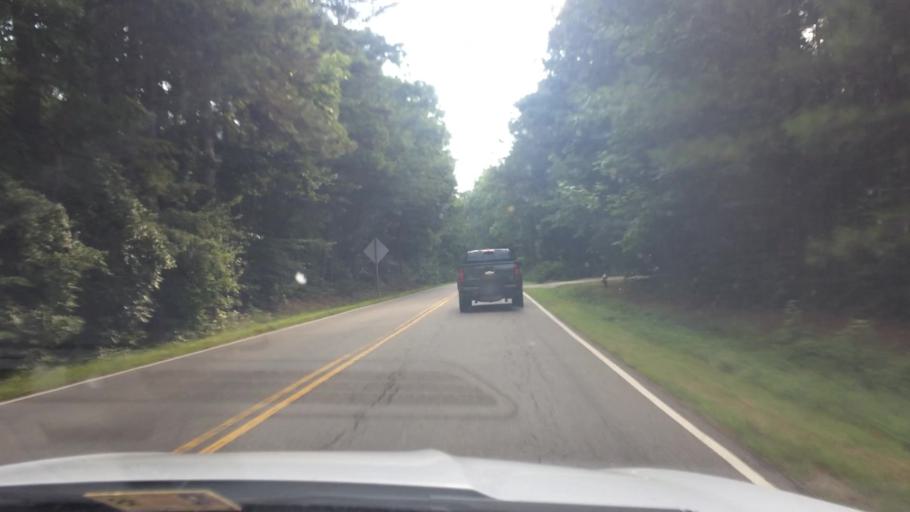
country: US
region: Virginia
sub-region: City of Williamsburg
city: Williamsburg
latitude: 37.2725
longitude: -76.6373
